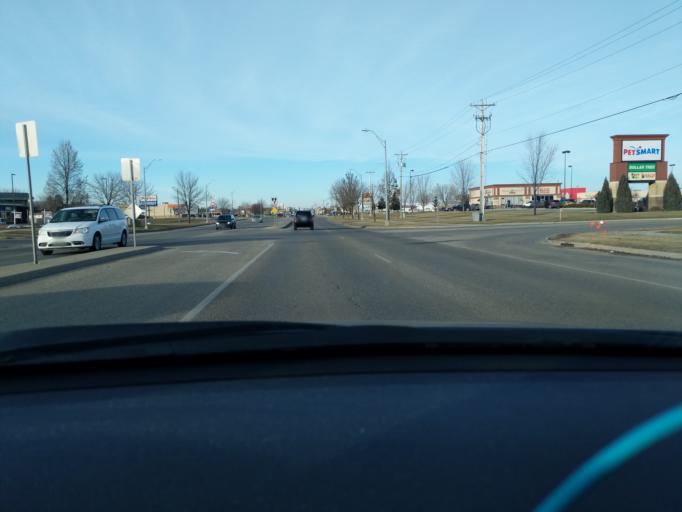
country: US
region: Minnesota
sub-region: Kandiyohi County
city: Willmar
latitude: 45.0990
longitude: -95.0426
